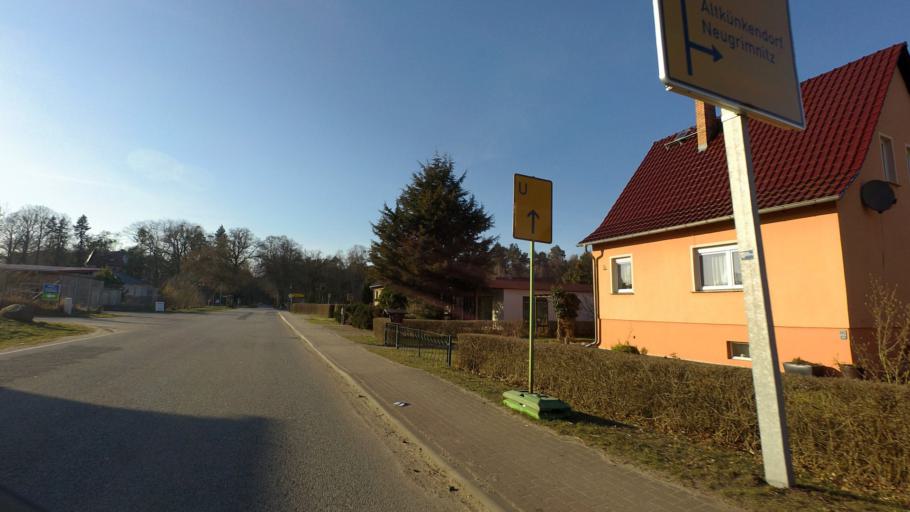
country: DE
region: Brandenburg
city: Althuttendorf
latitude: 52.9578
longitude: 13.7914
